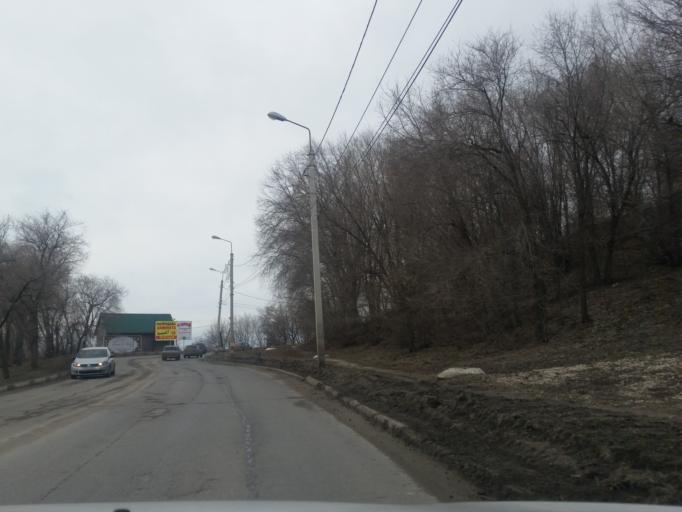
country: RU
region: Ulyanovsk
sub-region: Ulyanovskiy Rayon
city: Ulyanovsk
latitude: 54.3098
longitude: 48.4056
